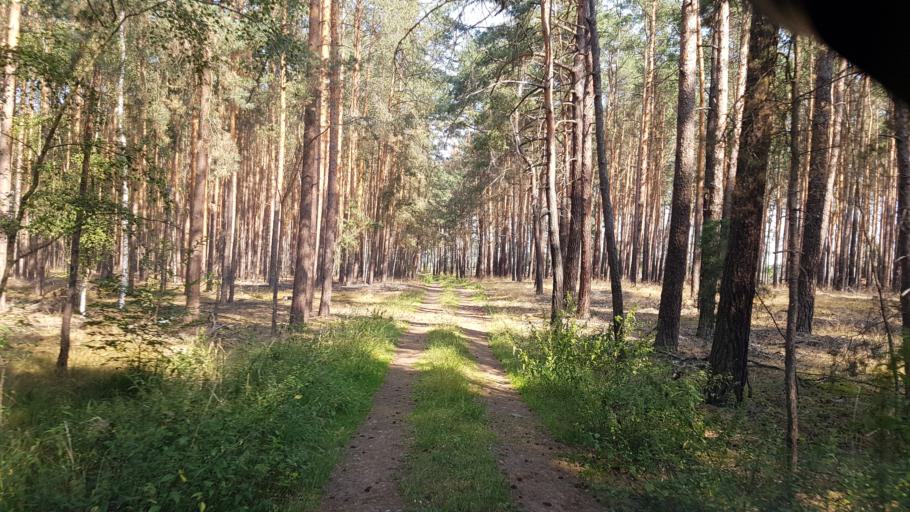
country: DE
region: Brandenburg
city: Cottbus
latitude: 51.7045
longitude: 14.4137
